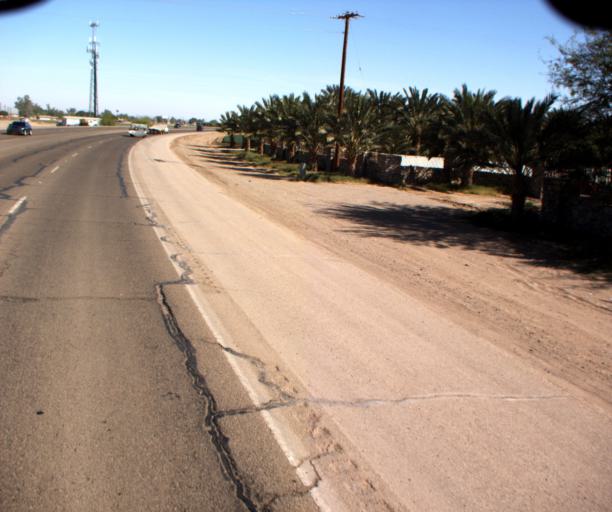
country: US
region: Arizona
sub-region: Yuma County
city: San Luis
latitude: 32.5460
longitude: -114.7868
